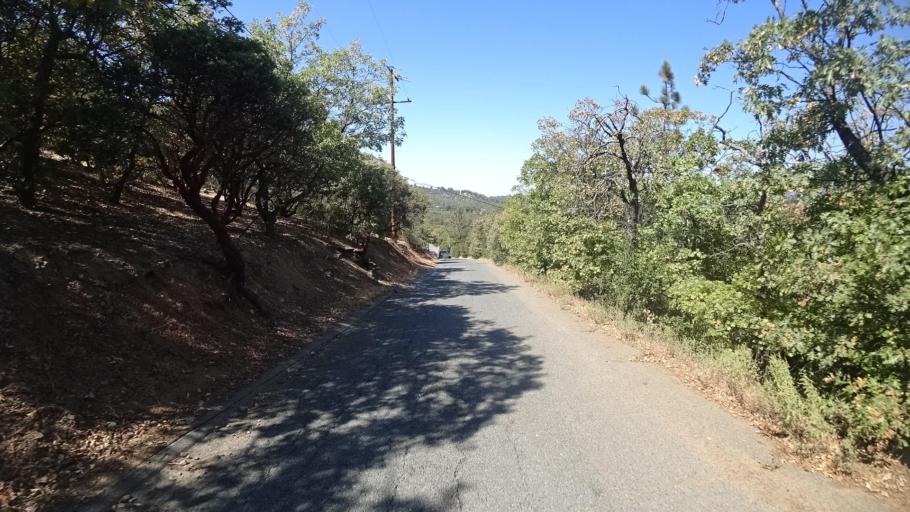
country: US
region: California
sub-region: San Diego County
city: Julian
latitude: 33.0832
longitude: -116.5875
